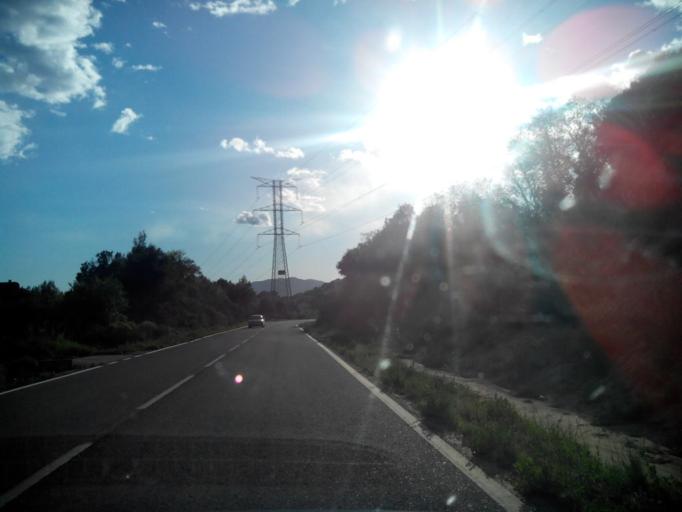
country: ES
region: Catalonia
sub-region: Provincia de Tarragona
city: Vilaplana
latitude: 41.2241
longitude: 1.0568
